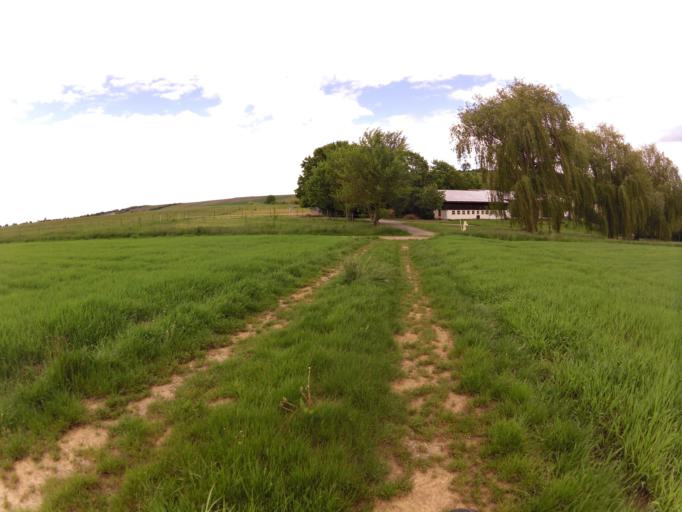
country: DE
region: Bavaria
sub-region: Regierungsbezirk Unterfranken
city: Volkach
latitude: 49.8806
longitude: 10.2440
